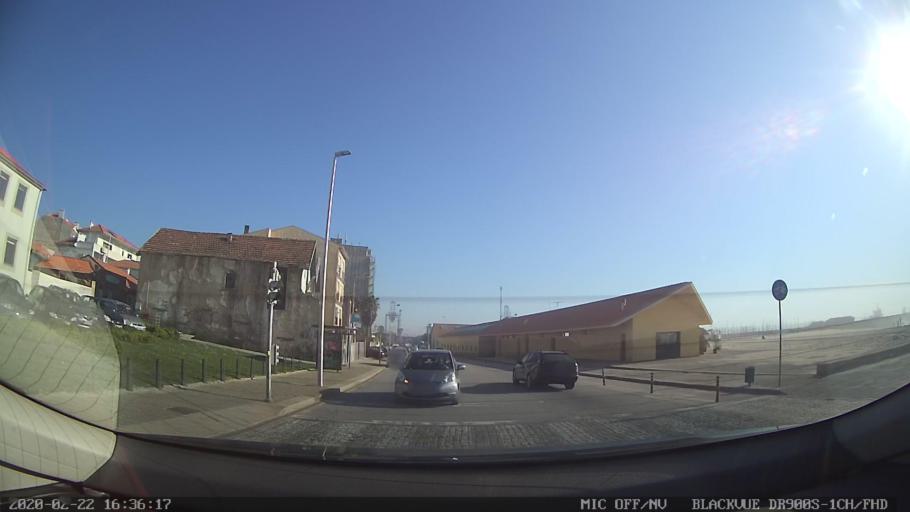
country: PT
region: Porto
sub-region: Matosinhos
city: Leca da Palmeira
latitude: 41.1894
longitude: -8.7045
